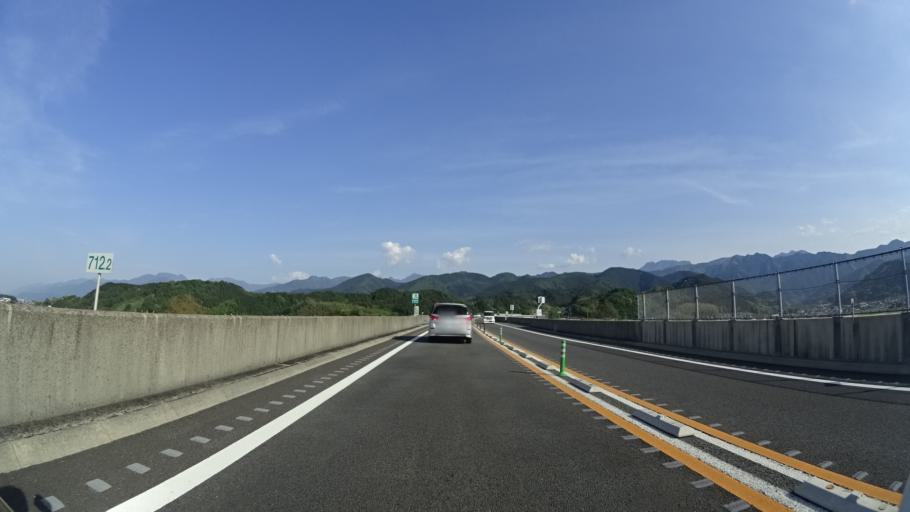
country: JP
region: Ehime
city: Saijo
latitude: 33.8925
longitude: 133.0840
